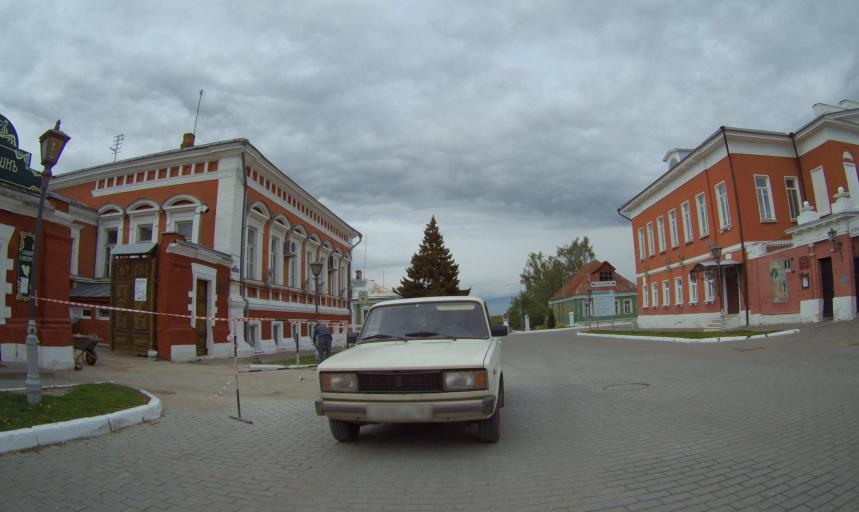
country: RU
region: Moskovskaya
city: Kolomna
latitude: 55.1049
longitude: 38.7543
